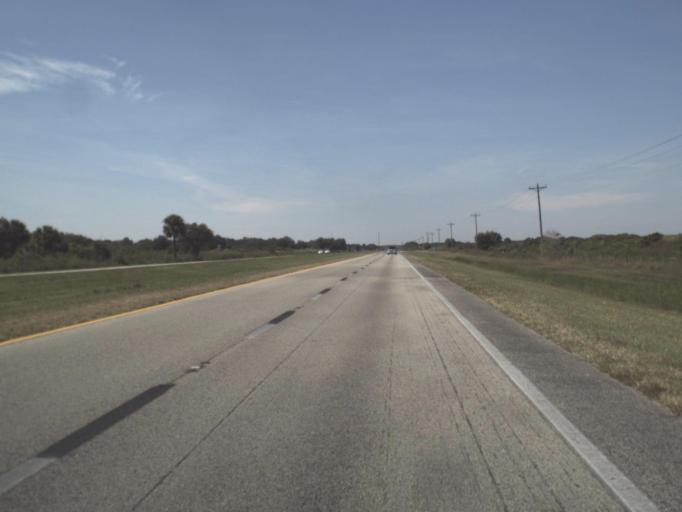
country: US
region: Florida
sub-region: Glades County
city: Moore Haven
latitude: 26.9094
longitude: -81.2709
